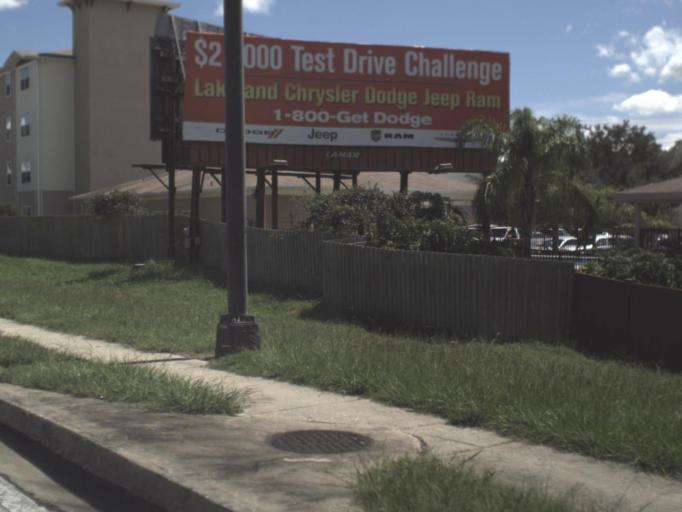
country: US
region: Florida
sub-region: Polk County
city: Lakeland
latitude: 28.0548
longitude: -81.9677
